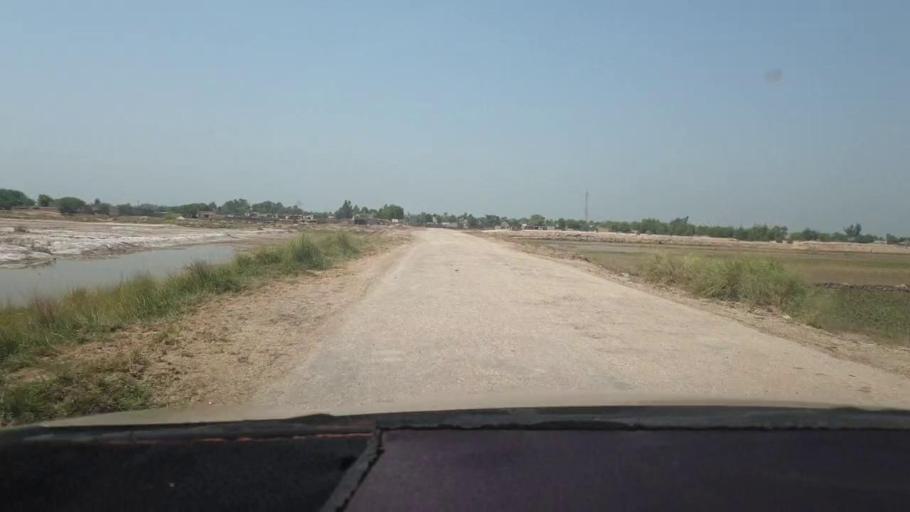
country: PK
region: Sindh
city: Miro Khan
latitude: 27.6665
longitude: 68.0679
